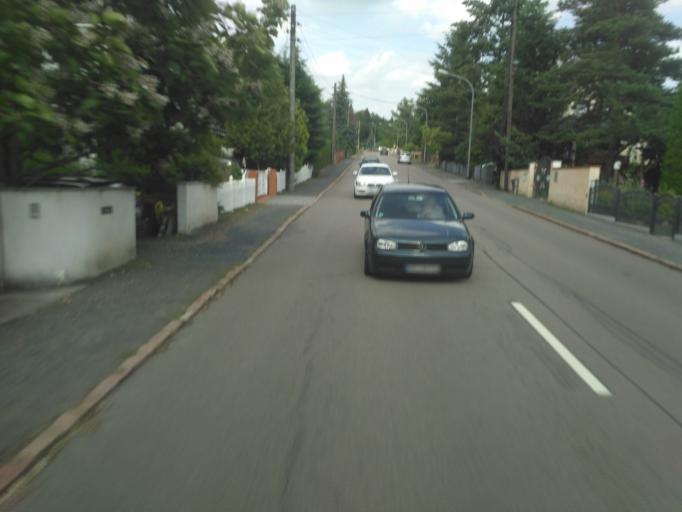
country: DE
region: Saxony
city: Weinbohla
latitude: 51.1641
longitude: 13.5789
